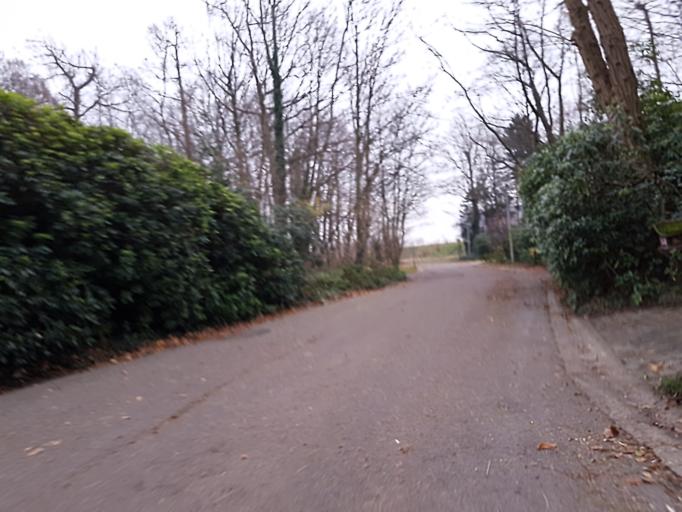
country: BE
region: Flanders
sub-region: Provincie Antwerpen
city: Willebroek
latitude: 51.0493
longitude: 4.3714
